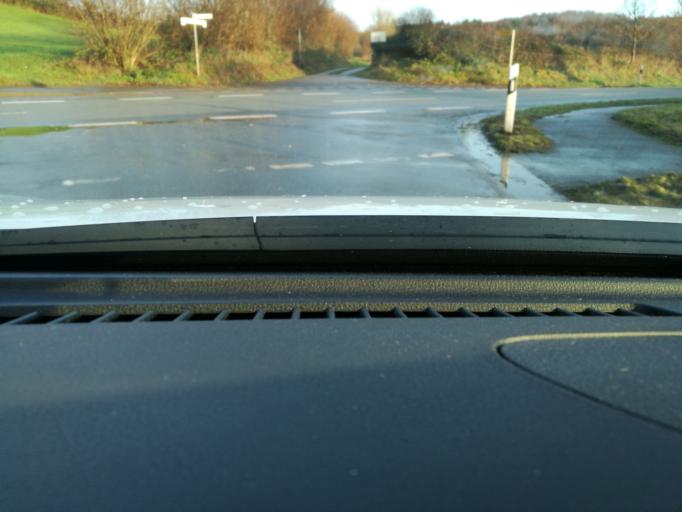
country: DE
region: Schleswig-Holstein
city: Holzbunge
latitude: 54.4065
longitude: 9.6788
